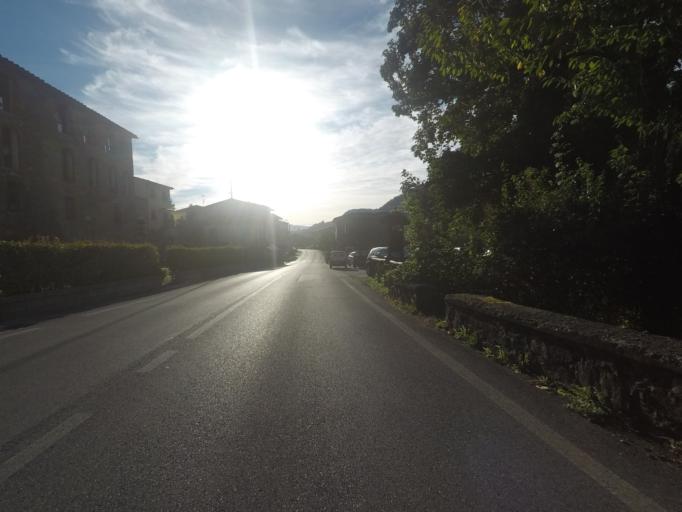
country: IT
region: Tuscany
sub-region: Provincia di Lucca
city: Pescaglia
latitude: 43.9524
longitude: 10.4308
